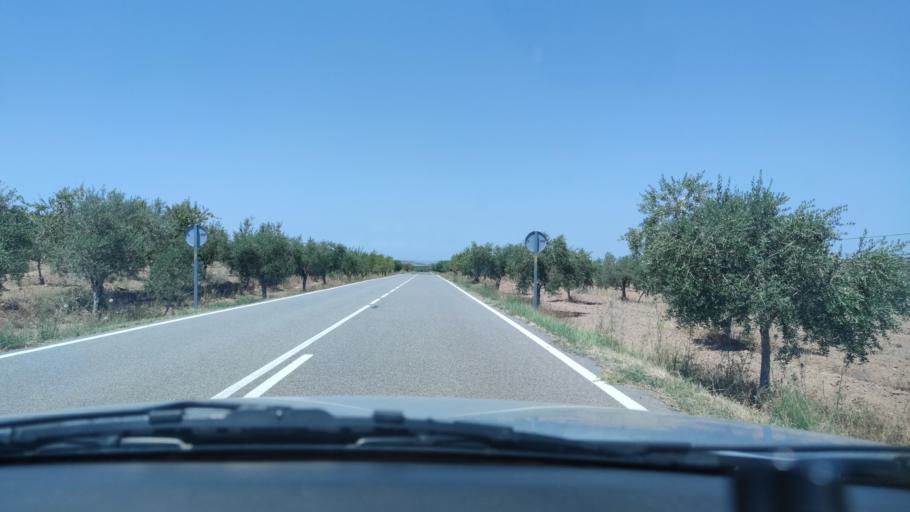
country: ES
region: Catalonia
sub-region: Provincia de Lleida
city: Alcano
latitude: 41.4460
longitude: 0.6404
